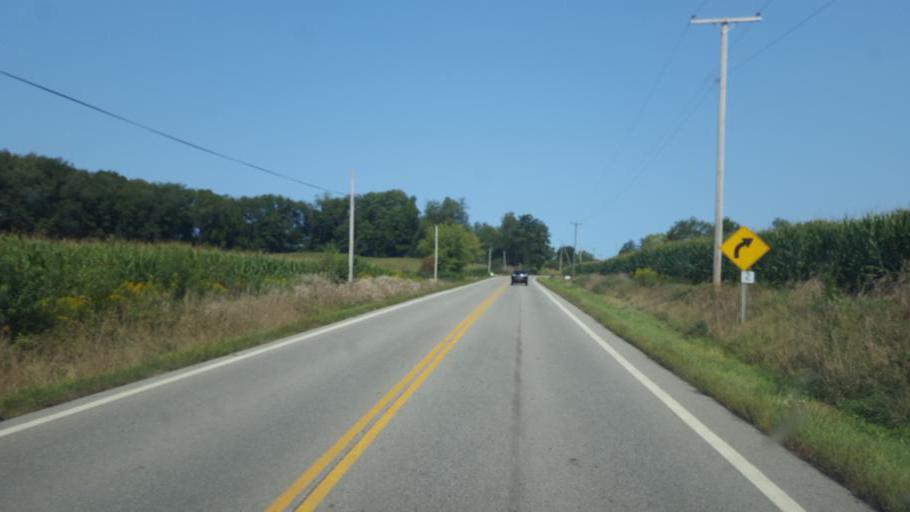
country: US
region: Ohio
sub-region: Wayne County
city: Shreve
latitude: 40.7020
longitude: -82.0989
